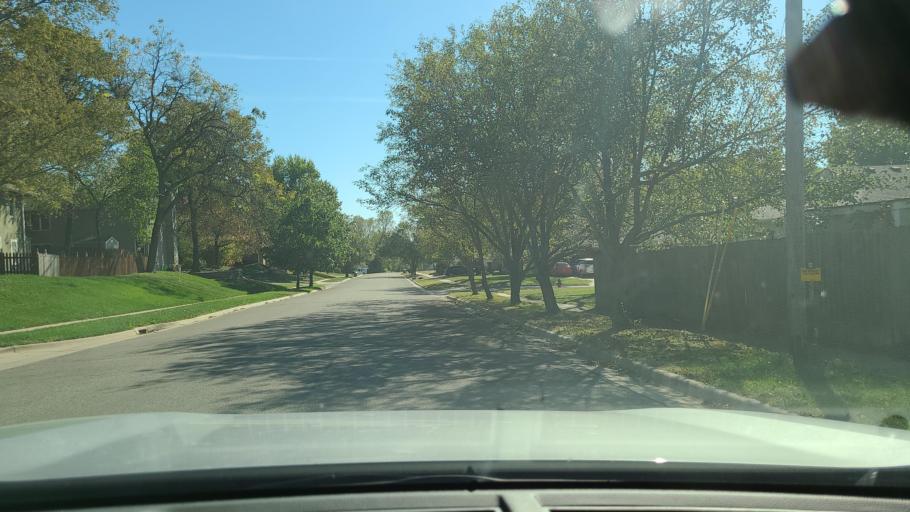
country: US
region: Kansas
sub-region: Shawnee County
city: Topeka
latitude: 38.9986
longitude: -95.7212
